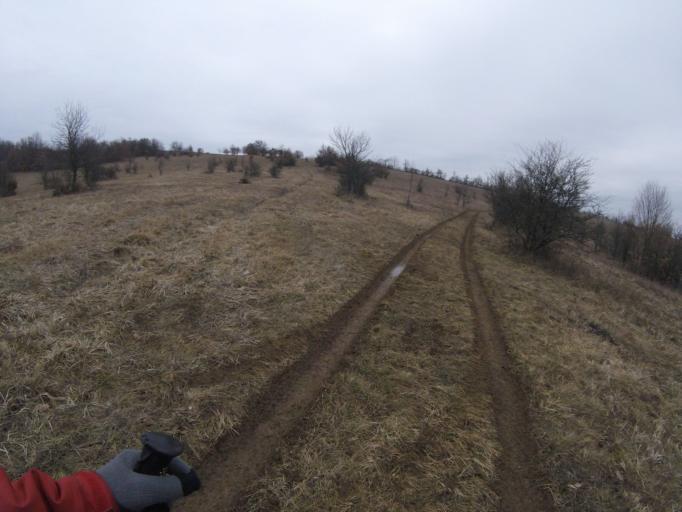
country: HU
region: Borsod-Abauj-Zemplen
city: Rudabanya
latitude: 48.4528
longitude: 20.6090
